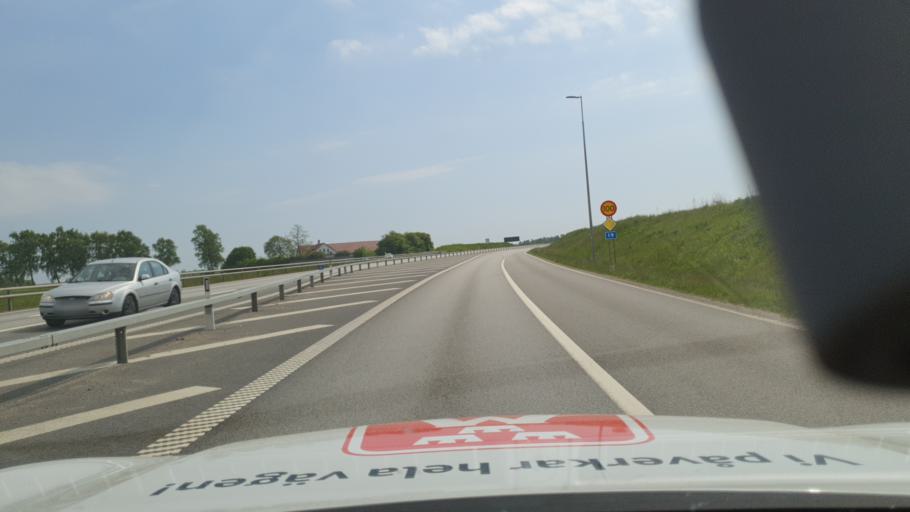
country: SE
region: Skane
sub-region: Ystads Kommun
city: Kopingebro
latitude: 55.4759
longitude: 13.8826
